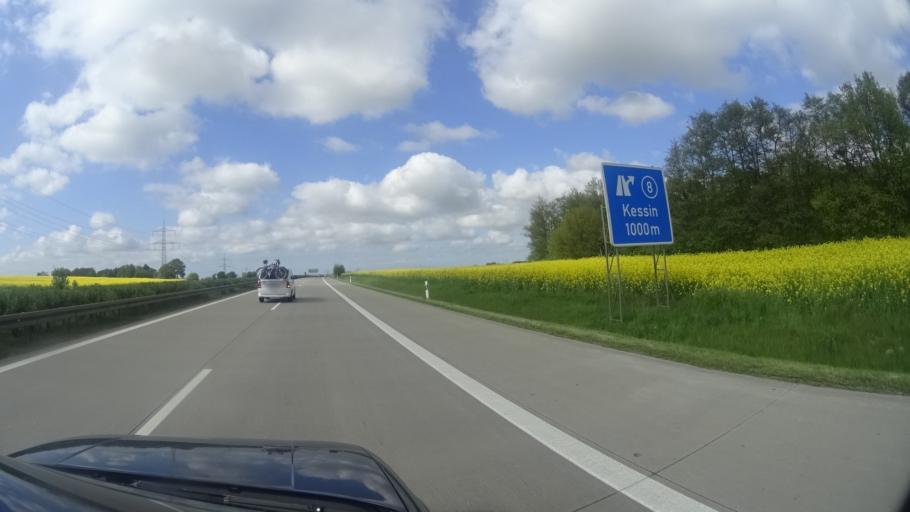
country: DE
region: Mecklenburg-Vorpommern
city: Roggentin
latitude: 54.0388
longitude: 12.1990
